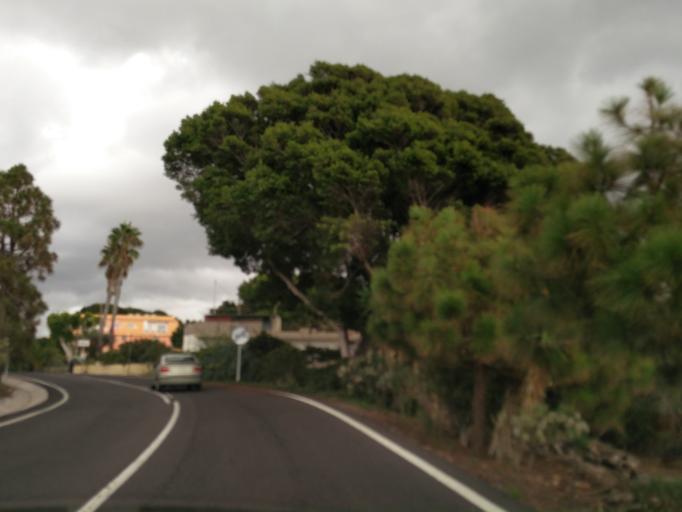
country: ES
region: Canary Islands
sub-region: Provincia de Santa Cruz de Tenerife
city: Arona
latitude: 28.0923
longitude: -16.6885
